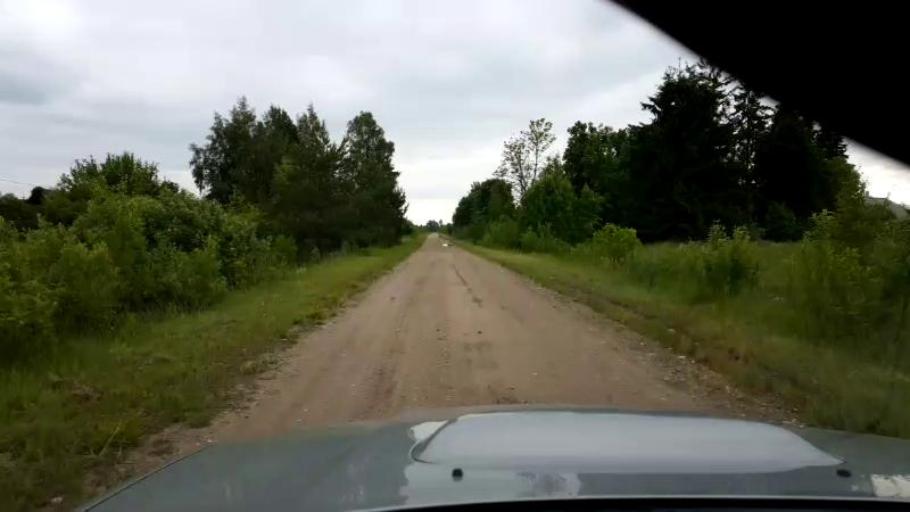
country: EE
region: Paernumaa
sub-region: Halinga vald
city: Parnu-Jaagupi
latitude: 58.5573
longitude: 24.5753
